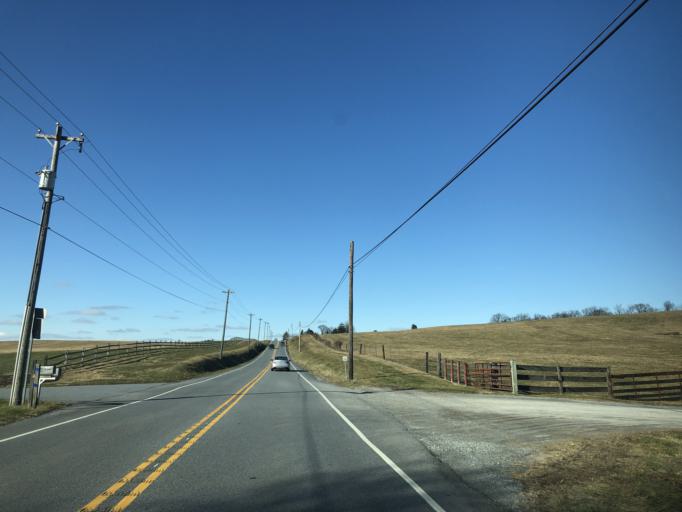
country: US
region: Pennsylvania
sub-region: Chester County
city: Upland
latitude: 39.9090
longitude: -75.8034
